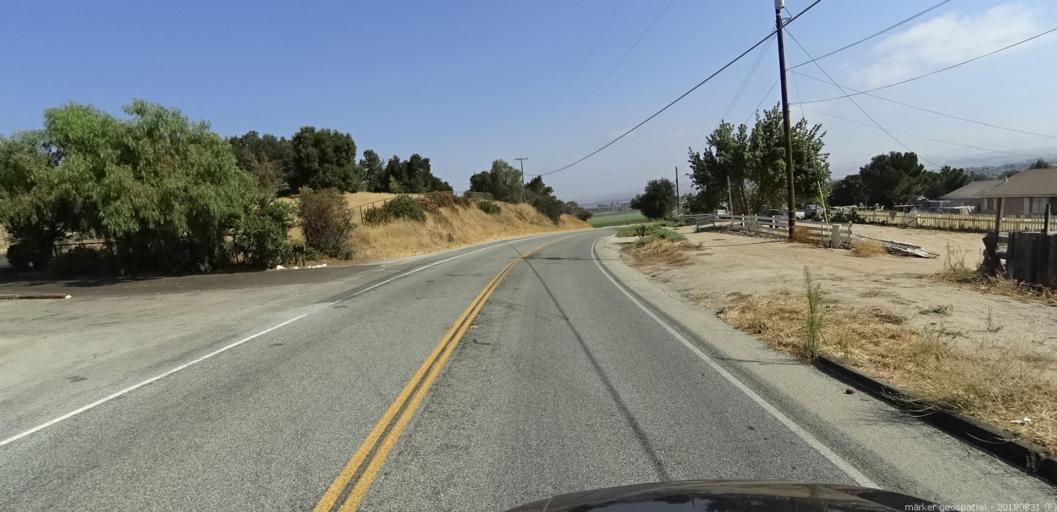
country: US
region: California
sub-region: Monterey County
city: King City
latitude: 36.1866
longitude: -121.1501
